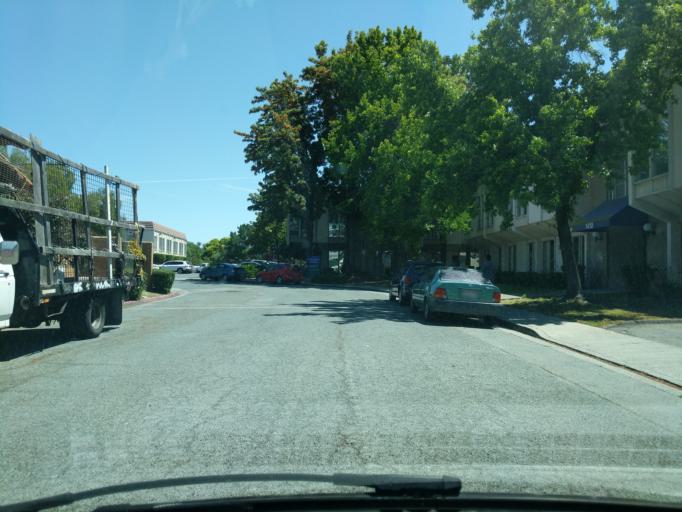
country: US
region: California
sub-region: Contra Costa County
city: Concord
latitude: 37.9695
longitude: -122.0499
